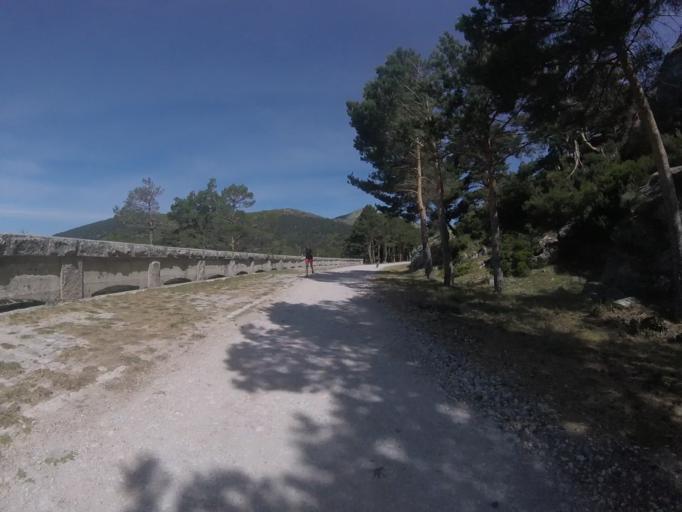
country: ES
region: Madrid
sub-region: Provincia de Madrid
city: Cercedilla
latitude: 40.7861
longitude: -4.0583
